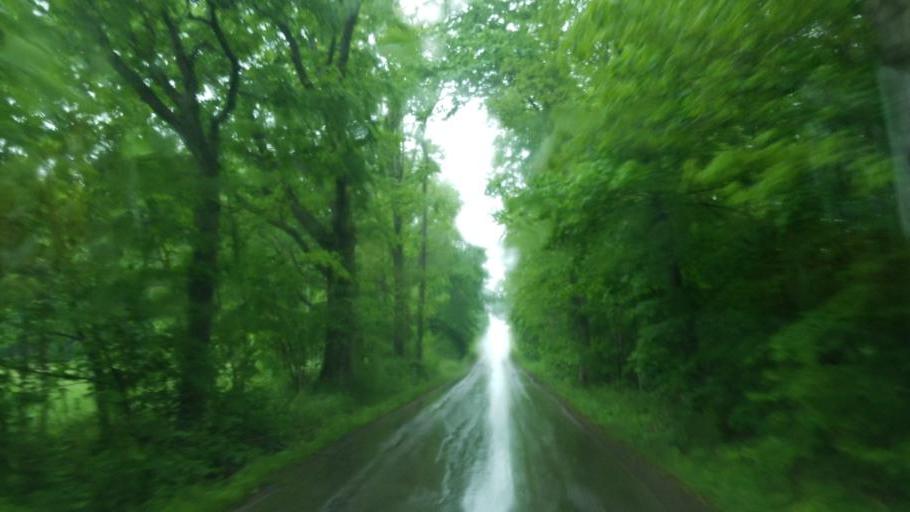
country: US
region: Ohio
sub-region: Knox County
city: Oak Hill
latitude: 40.3174
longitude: -82.2592
